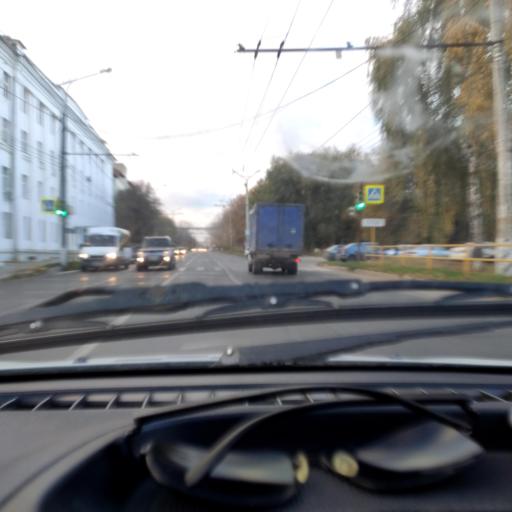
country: RU
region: Samara
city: Tol'yatti
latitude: 53.5233
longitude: 49.4340
